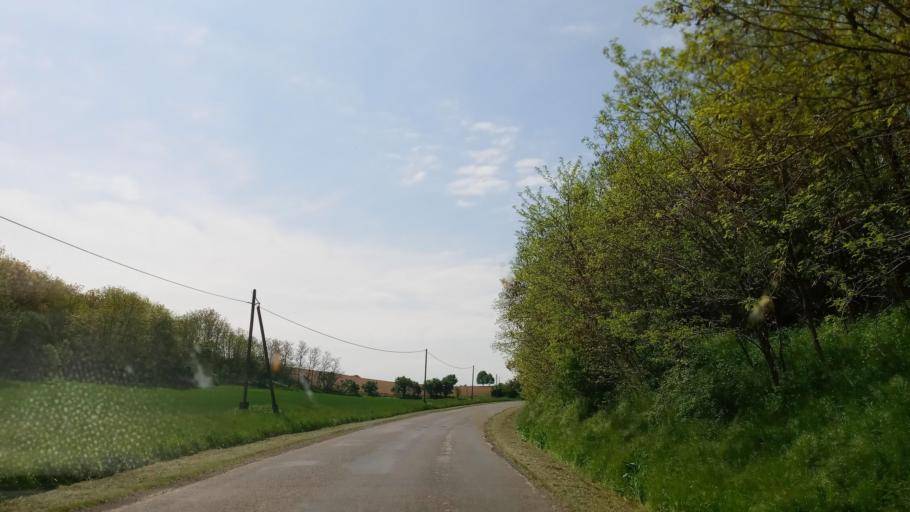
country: HU
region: Baranya
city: Boly
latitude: 45.8968
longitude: 18.5905
